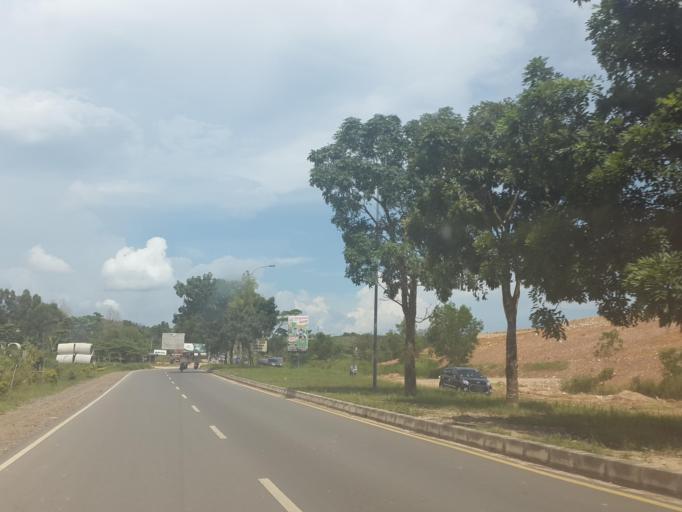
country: SG
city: Singapore
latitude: 1.0286
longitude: 104.0060
